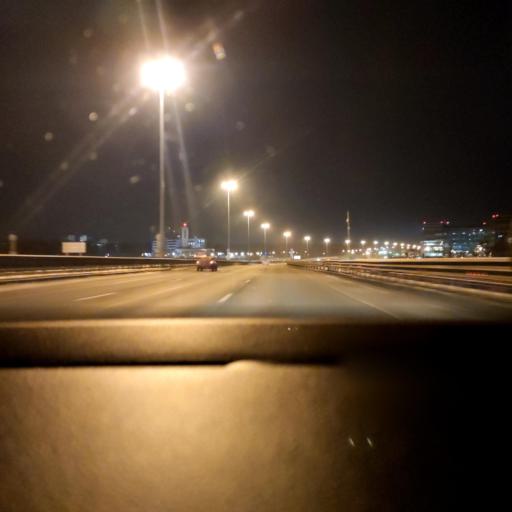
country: RU
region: Moscow
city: Khimki
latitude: 55.9548
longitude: 37.4140
